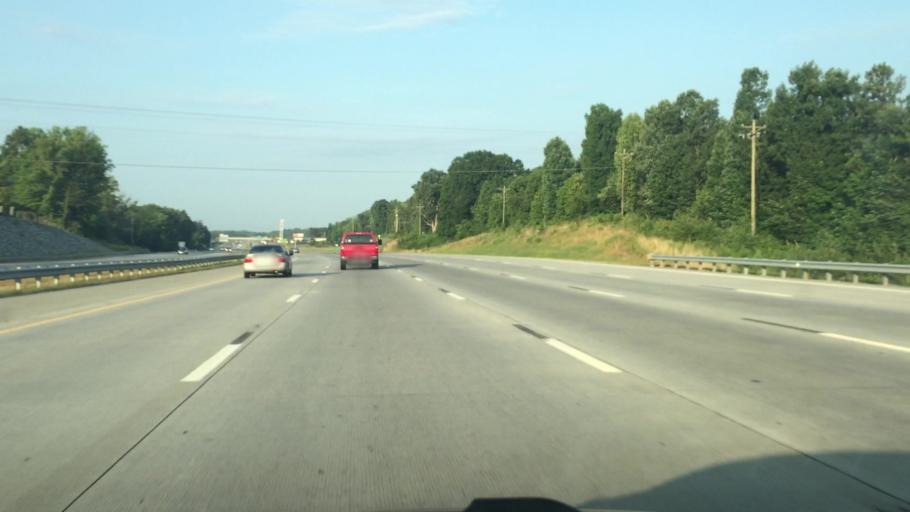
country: US
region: North Carolina
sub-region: Davidson County
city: Tyro
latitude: 35.7634
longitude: -80.3380
